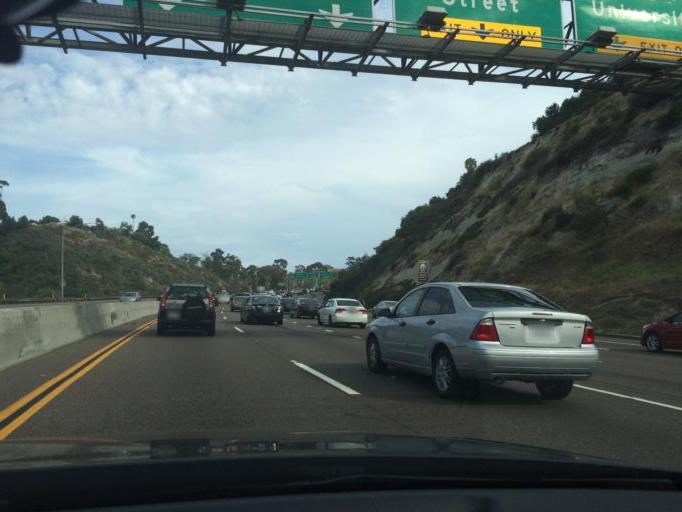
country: US
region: California
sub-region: San Diego County
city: San Diego
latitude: 32.7572
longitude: -117.1597
